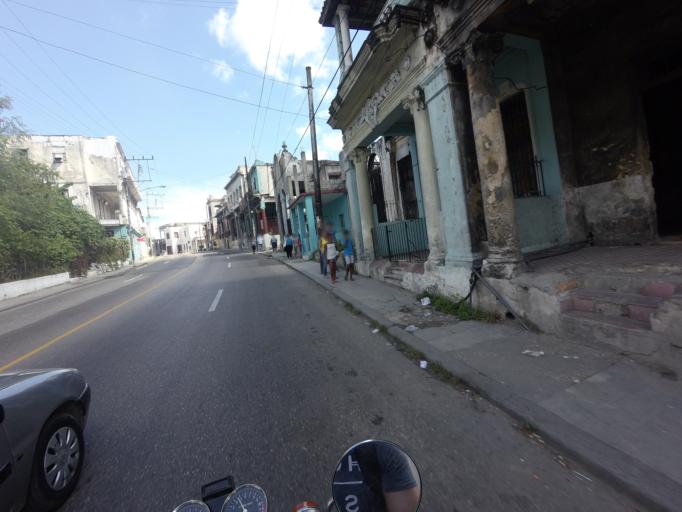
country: CU
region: La Habana
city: Diez de Octubre
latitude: 23.0982
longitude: -82.3621
